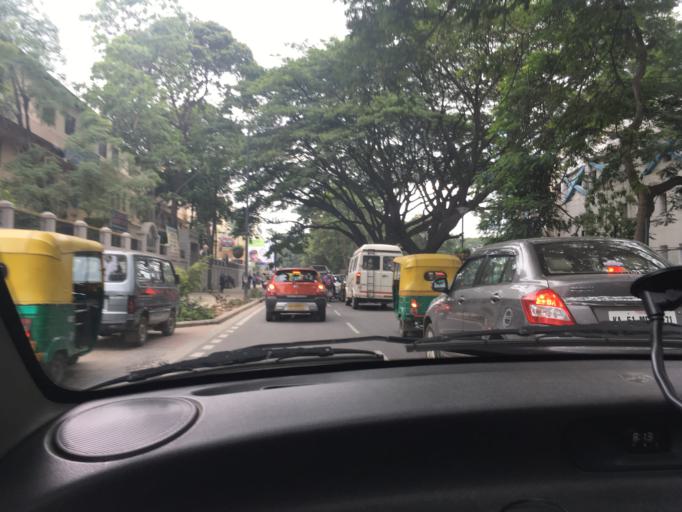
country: IN
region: Karnataka
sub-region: Bangalore Urban
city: Bangalore
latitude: 12.9699
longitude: 77.5944
